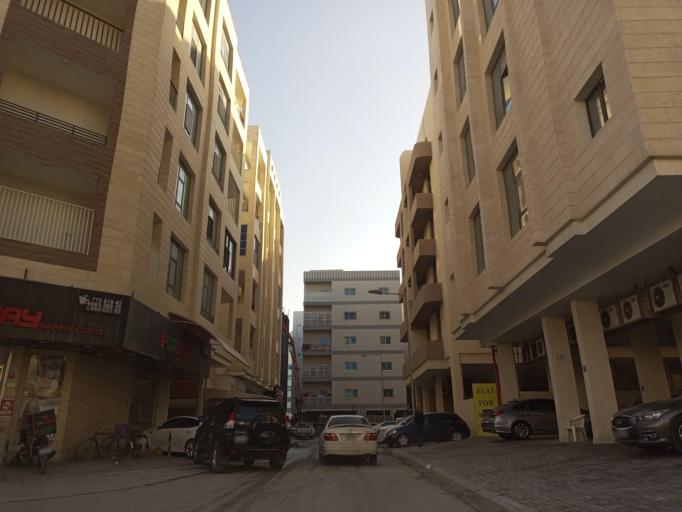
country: BH
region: Muharraq
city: Al Hadd
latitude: 26.2297
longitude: 50.6467
